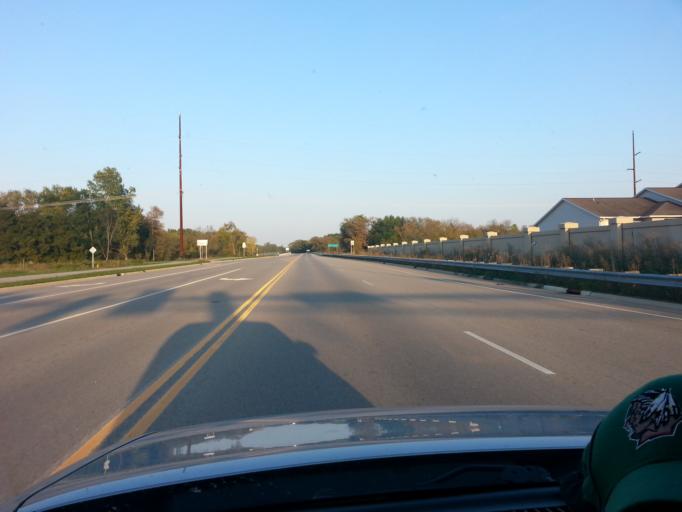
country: US
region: Minnesota
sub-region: Olmsted County
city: Rochester
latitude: 43.9927
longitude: -92.4421
